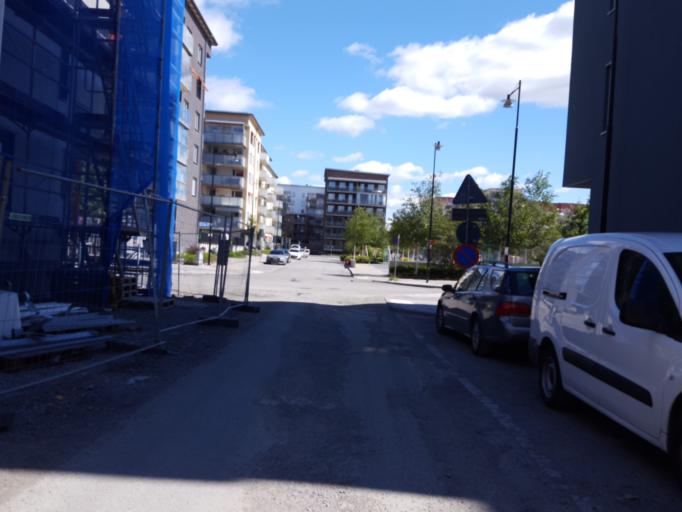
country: SE
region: Uppsala
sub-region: Uppsala Kommun
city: Uppsala
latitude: 59.8484
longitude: 17.6537
